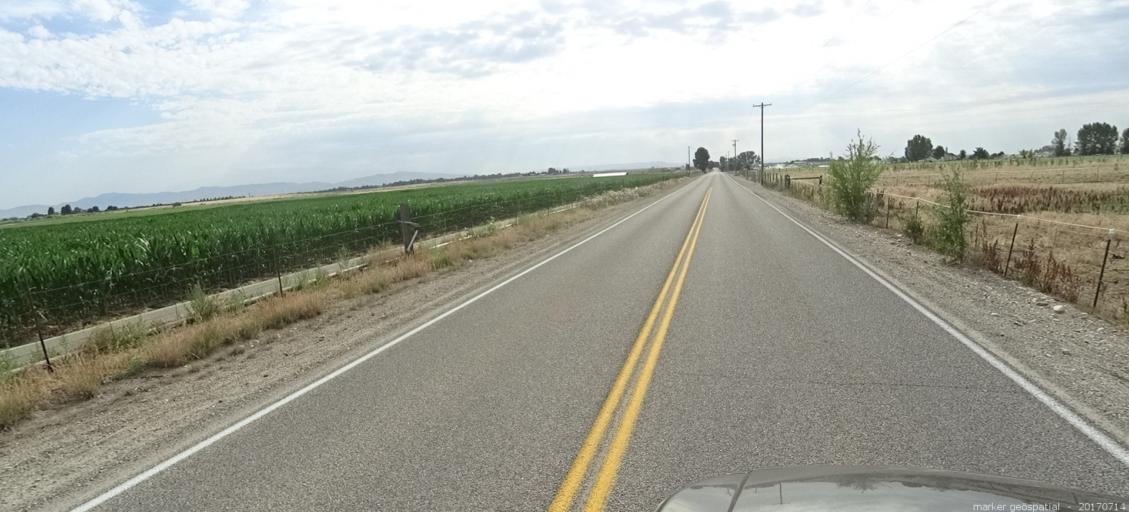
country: US
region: Idaho
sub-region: Ada County
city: Kuna
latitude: 43.4736
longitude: -116.3538
